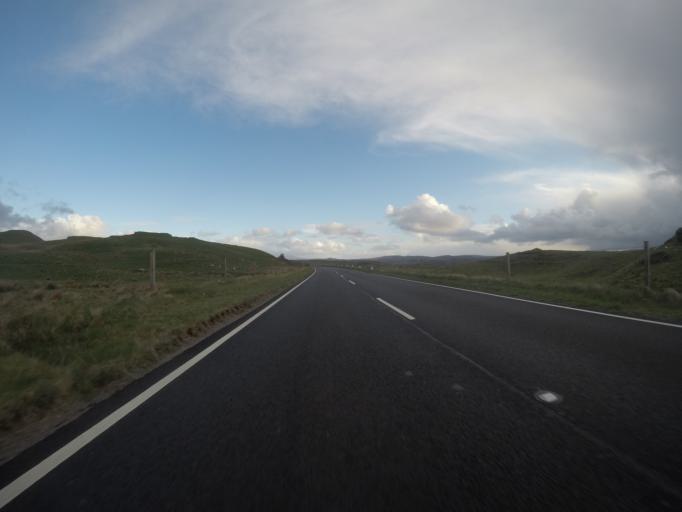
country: GB
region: Scotland
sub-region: Highland
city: Portree
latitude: 57.5433
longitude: -6.3650
